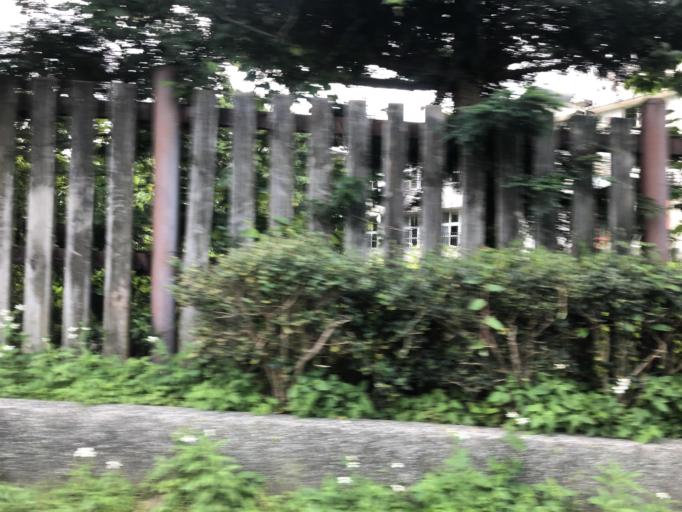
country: TW
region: Taiwan
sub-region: Keelung
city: Keelung
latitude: 25.2242
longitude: 121.6377
